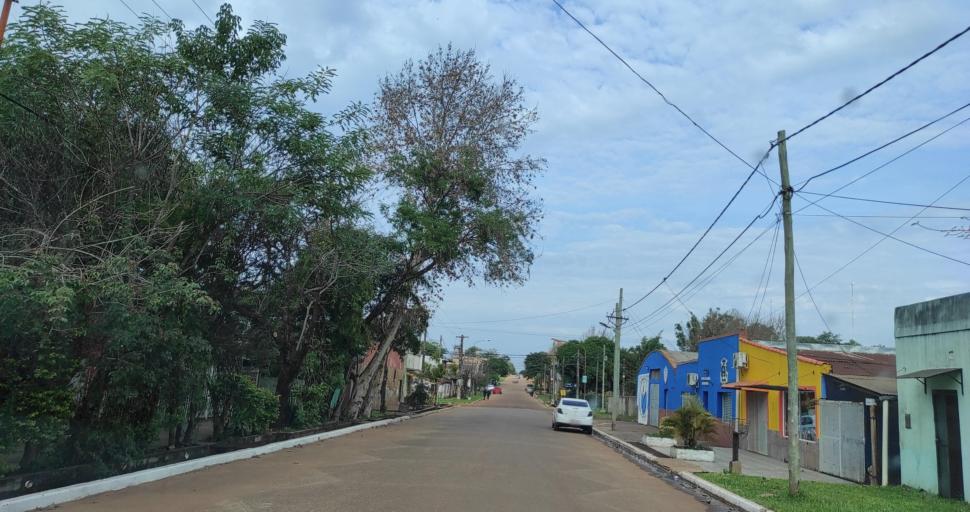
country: AR
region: Corrientes
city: Santo Tome
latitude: -28.5534
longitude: -56.0374
